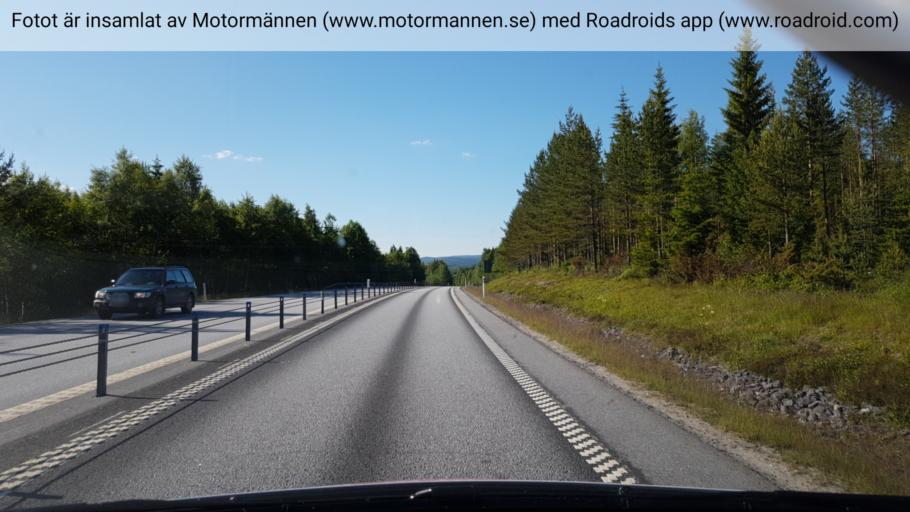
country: SE
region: Vaesterbotten
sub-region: Vannas Kommun
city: Vannasby
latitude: 63.9052
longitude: 19.8924
